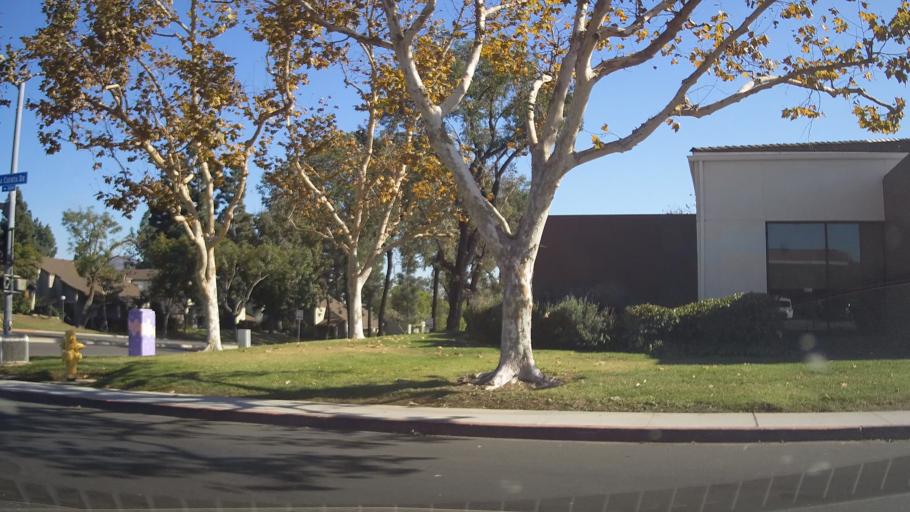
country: US
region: California
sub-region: San Diego County
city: La Mesa
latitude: 32.8212
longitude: -117.0982
